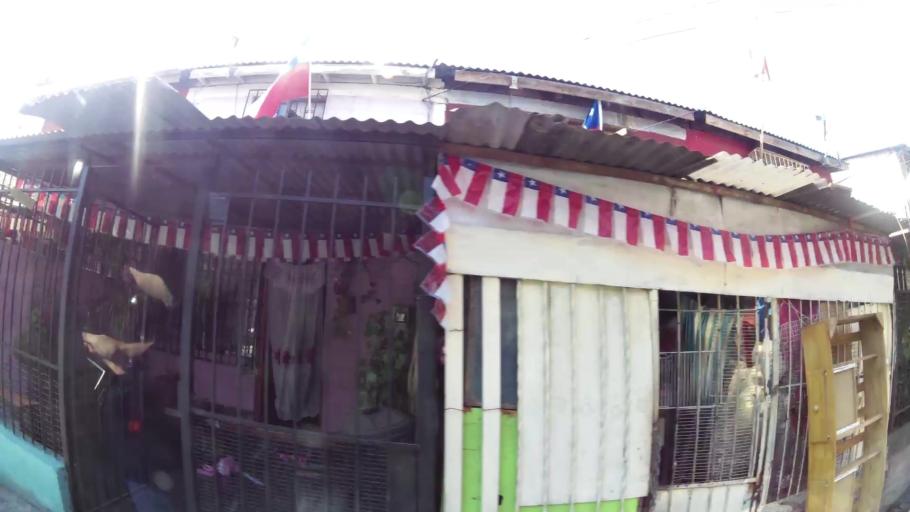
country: CL
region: Santiago Metropolitan
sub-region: Provincia de Santiago
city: La Pintana
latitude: -33.5611
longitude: -70.6386
